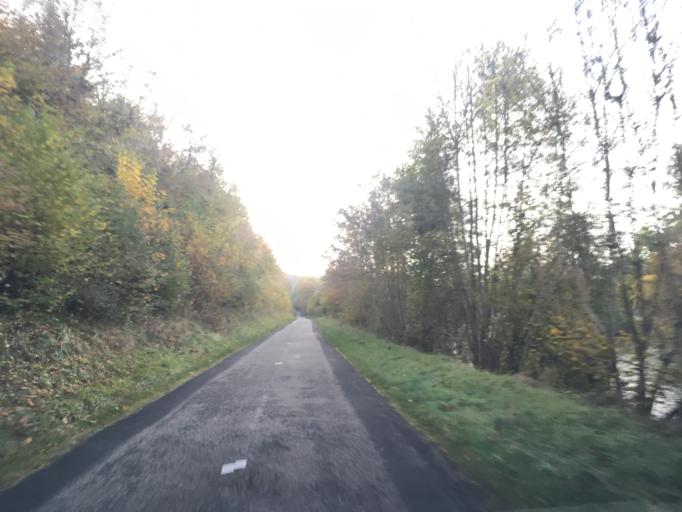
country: FR
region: Haute-Normandie
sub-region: Departement de l'Eure
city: Heudreville-sur-Eure
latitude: 49.1078
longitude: 1.2186
